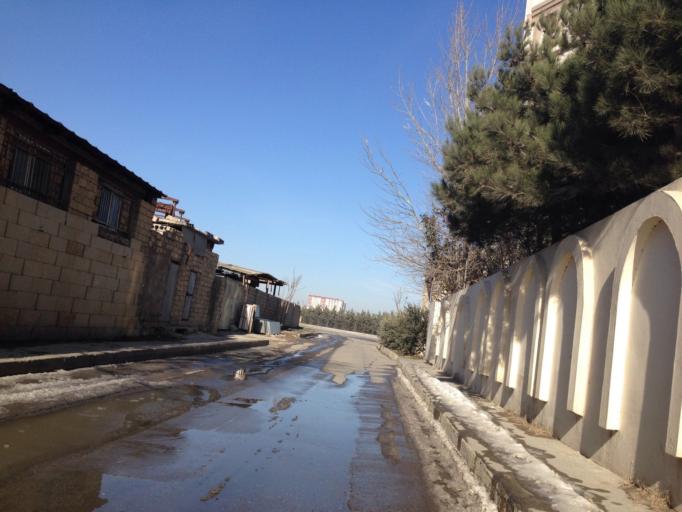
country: AZ
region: Baki
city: Baku
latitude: 40.4060
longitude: 49.8593
